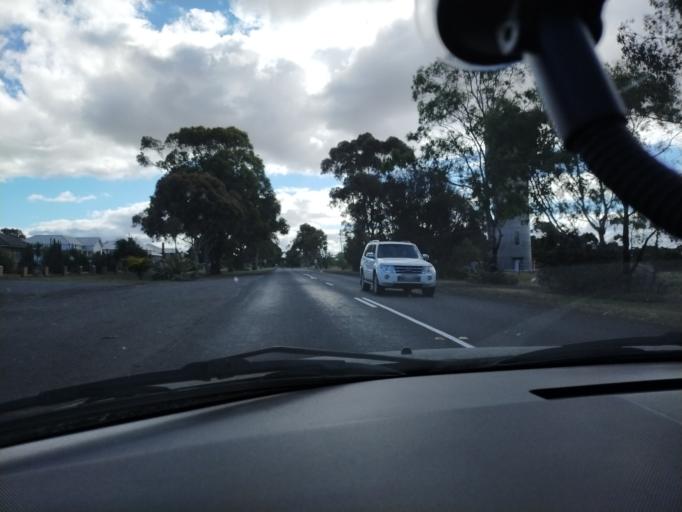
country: AU
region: Victoria
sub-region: Colac-Otway
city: Colac
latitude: -38.0281
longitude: 143.6409
